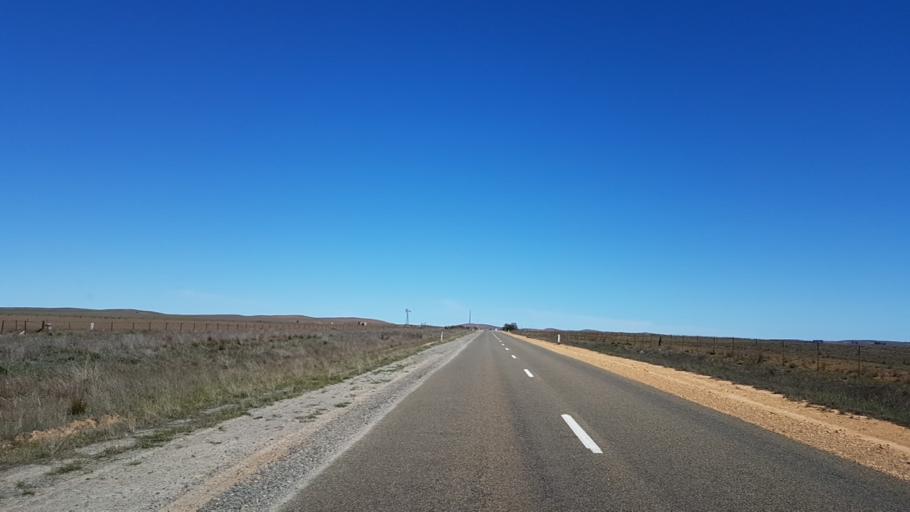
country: AU
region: South Australia
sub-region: Peterborough
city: Peterborough
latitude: -33.0085
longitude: 138.8527
